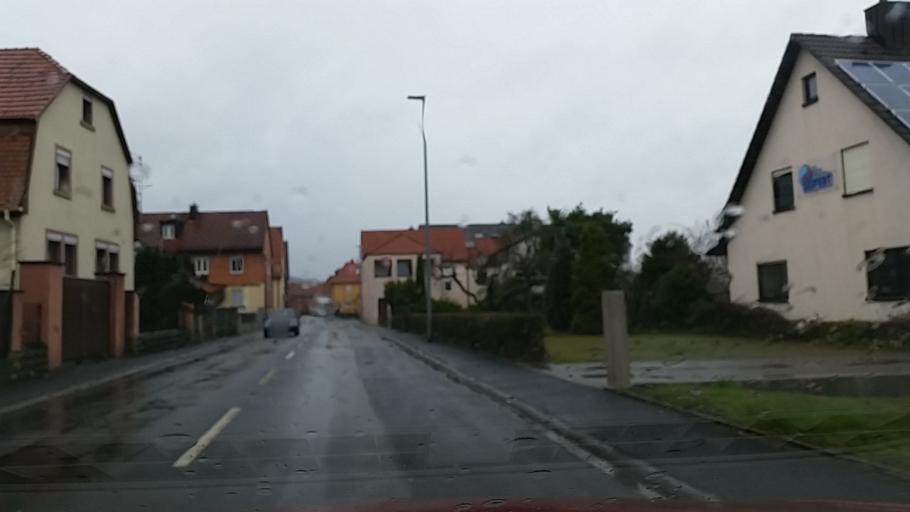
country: DE
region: Bavaria
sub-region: Regierungsbezirk Unterfranken
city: Zellingen
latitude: 49.8952
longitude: 9.8205
